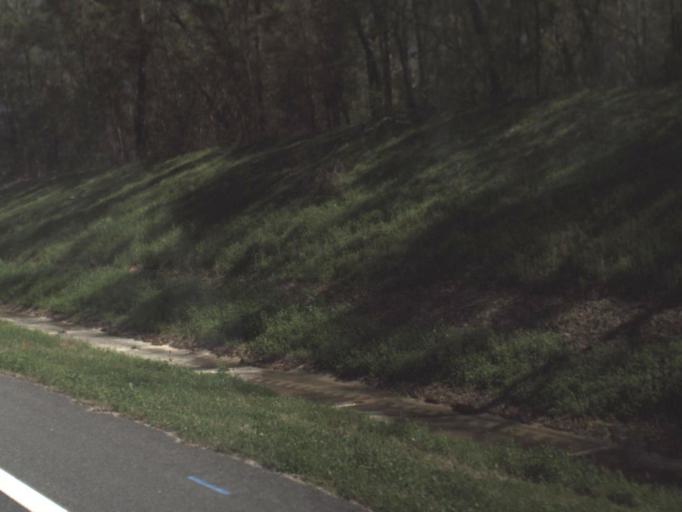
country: US
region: Florida
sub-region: Gadsden County
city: Quincy
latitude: 30.4825
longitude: -84.6242
